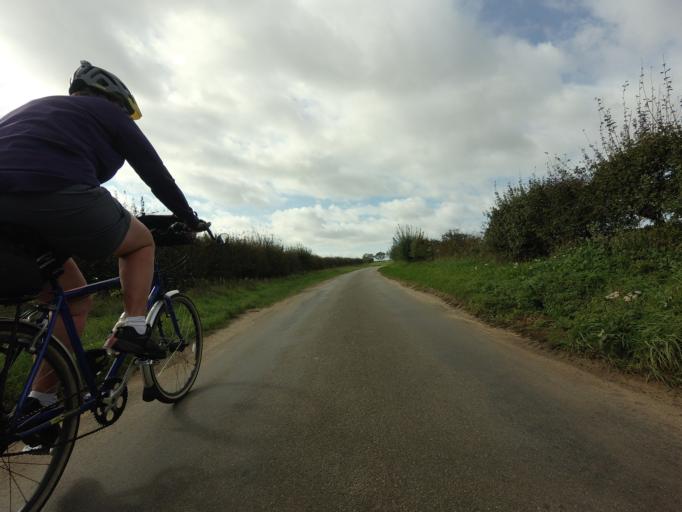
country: GB
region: England
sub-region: Norfolk
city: Hunstanton
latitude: 52.9361
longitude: 0.6569
